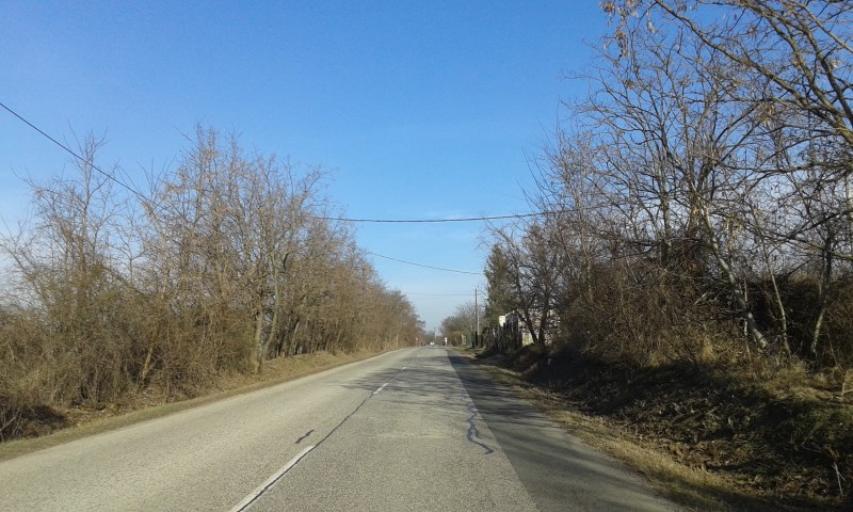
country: HU
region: Pest
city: Soskut
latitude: 47.4100
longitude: 18.8063
